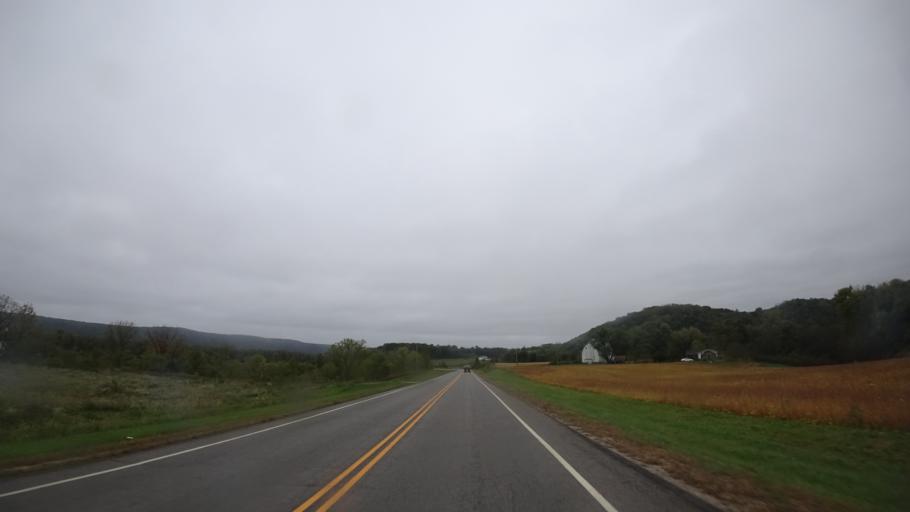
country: US
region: Wisconsin
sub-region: Crawford County
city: Prairie du Chien
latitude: 43.0480
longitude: -90.9846
